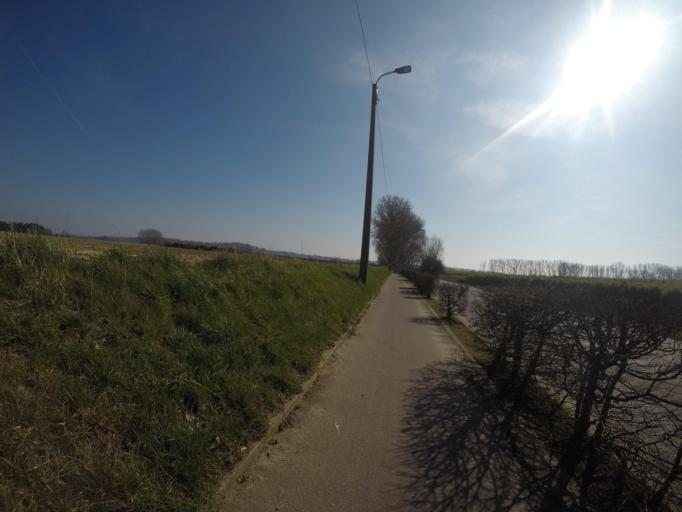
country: BE
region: Flanders
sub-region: Provincie Oost-Vlaanderen
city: Geraardsbergen
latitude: 50.7806
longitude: 3.8552
